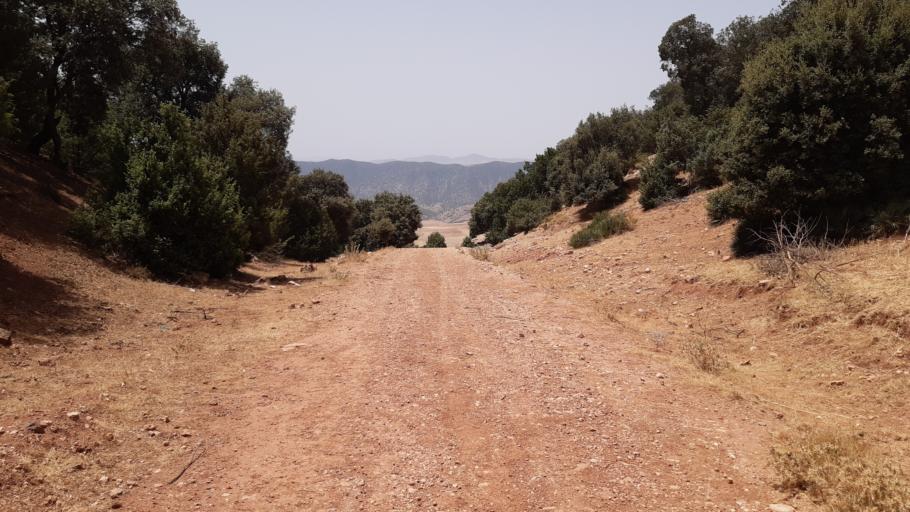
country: MA
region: Meknes-Tafilalet
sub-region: Khenifra
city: Khenifra
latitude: 33.0441
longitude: -5.5139
